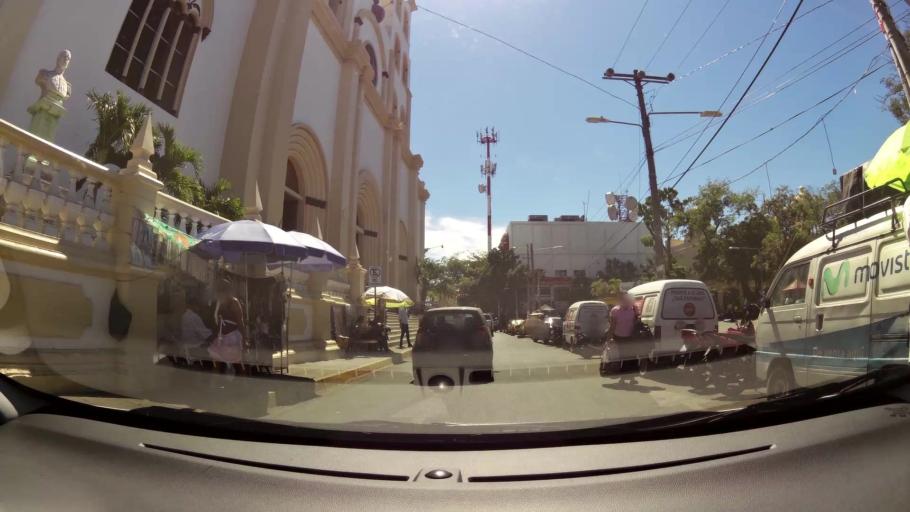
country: SV
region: San Miguel
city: San Miguel
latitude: 13.4832
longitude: -88.1751
